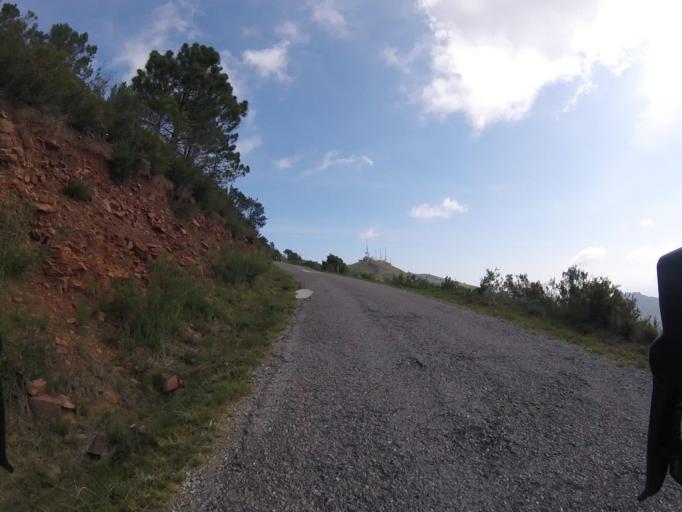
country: ES
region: Valencia
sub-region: Provincia de Castello
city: Benicassim
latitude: 40.0797
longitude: 0.0235
